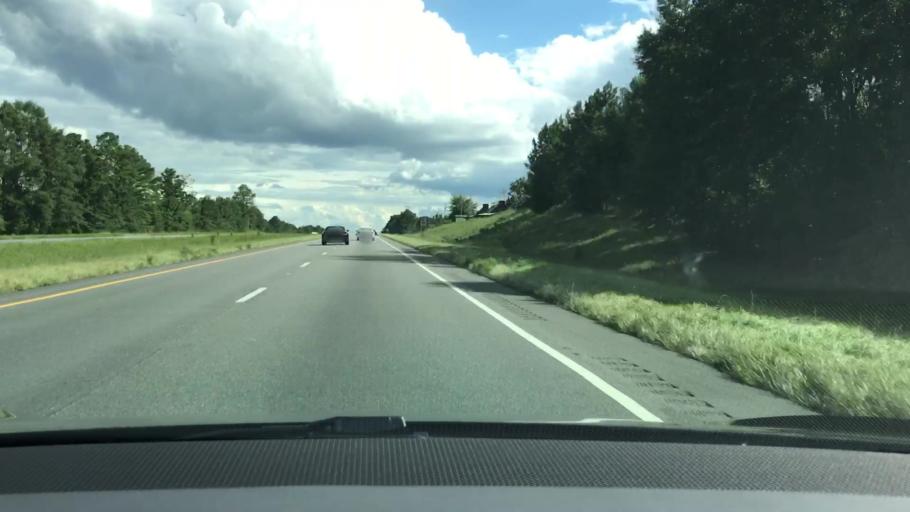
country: US
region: Alabama
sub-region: Pike County
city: Troy
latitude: 31.9040
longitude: -86.0115
